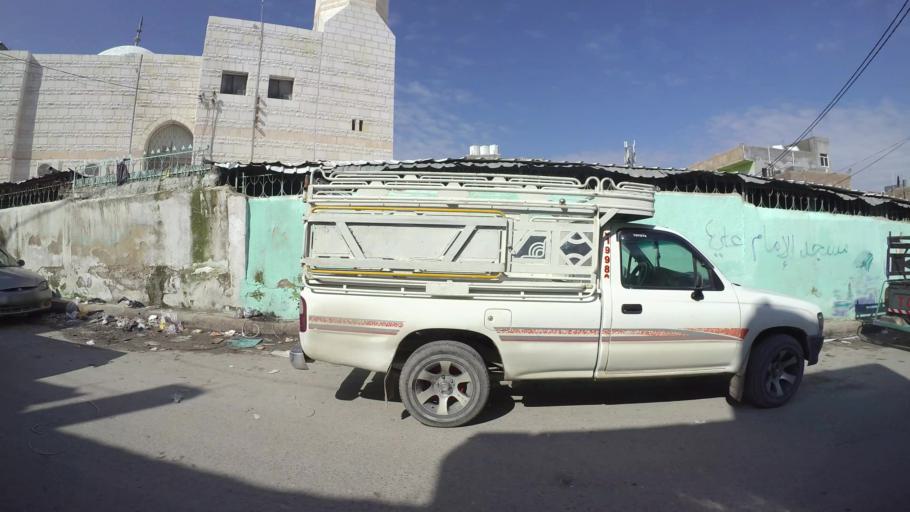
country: JO
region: Amman
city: Al Jubayhah
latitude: 32.0760
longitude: 35.8475
